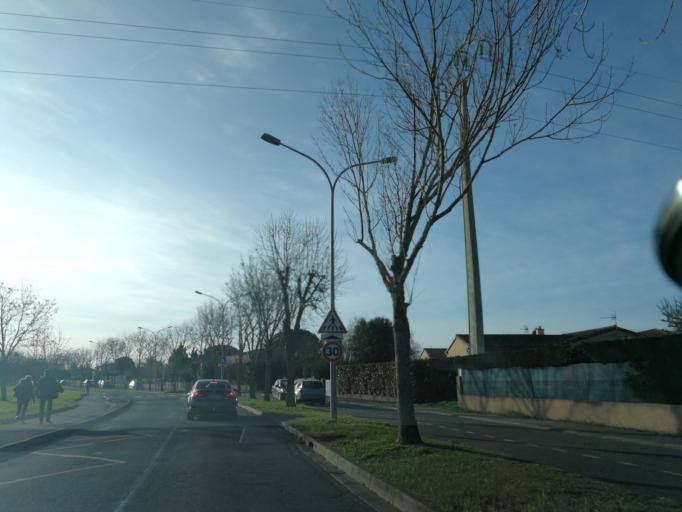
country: FR
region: Midi-Pyrenees
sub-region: Departement de la Haute-Garonne
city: L'Union
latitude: 43.6487
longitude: 1.4930
